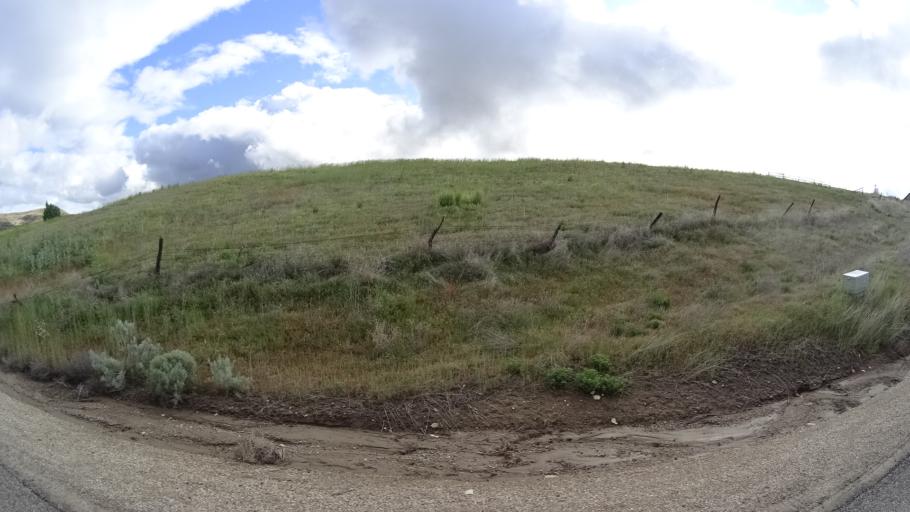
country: US
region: Idaho
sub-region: Ada County
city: Eagle
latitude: 43.7283
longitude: -116.2661
